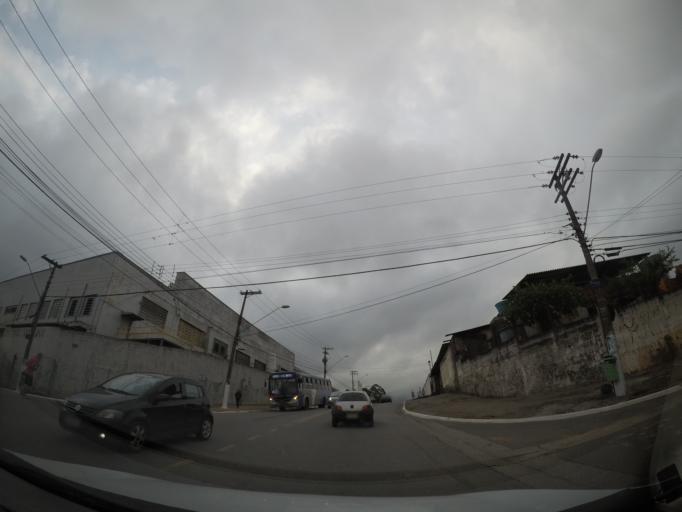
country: BR
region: Sao Paulo
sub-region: Aruja
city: Aruja
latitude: -23.4079
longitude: -46.3935
